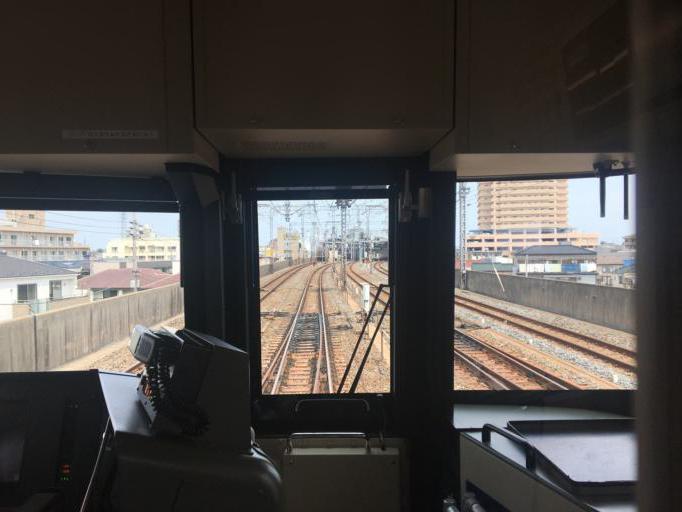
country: JP
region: Saitama
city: Koshigaya
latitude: 35.8993
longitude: 139.7807
